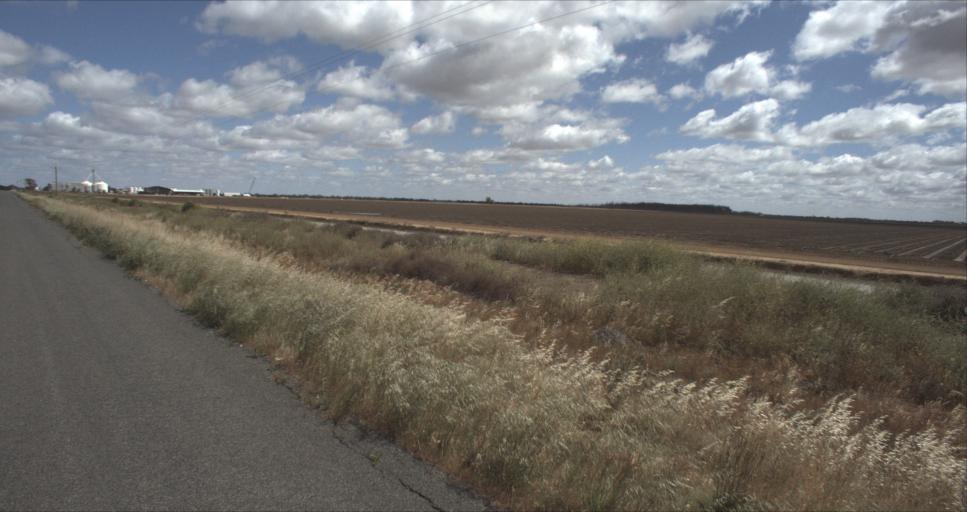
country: AU
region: New South Wales
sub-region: Murrumbidgee Shire
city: Darlington Point
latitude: -34.5772
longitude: 146.1874
